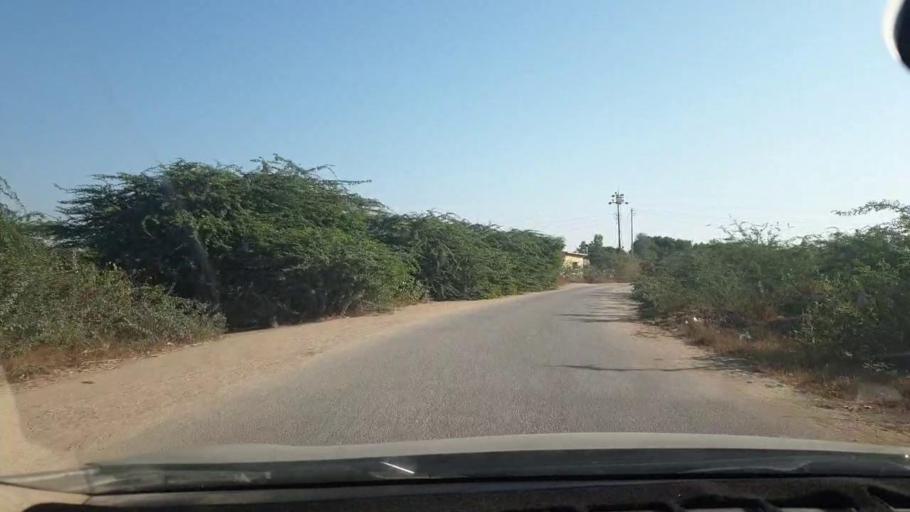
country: PK
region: Sindh
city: Malir Cantonment
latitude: 25.1758
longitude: 67.2038
